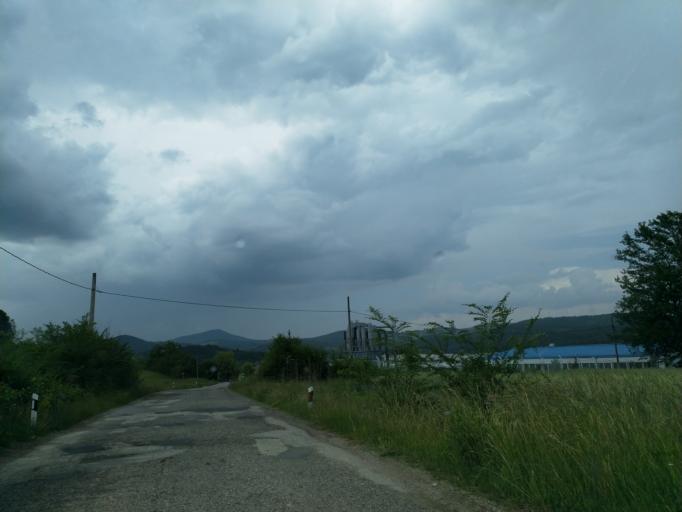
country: RS
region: Central Serbia
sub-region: Borski Okrug
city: Bor
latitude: 43.9965
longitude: 21.9785
